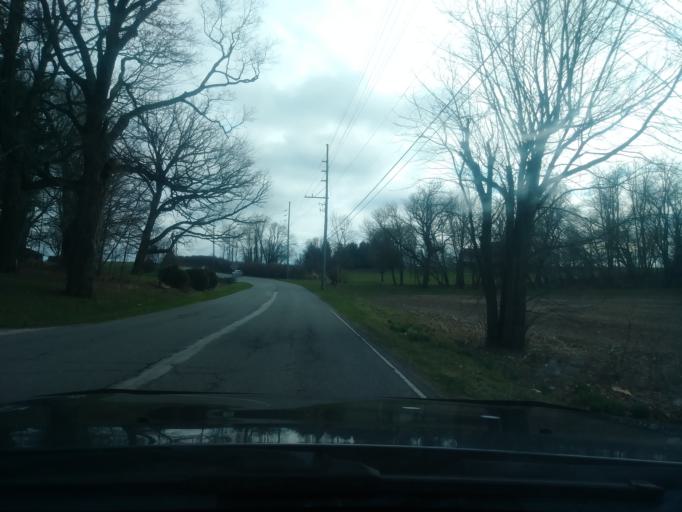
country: US
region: Indiana
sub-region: LaPorte County
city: LaPorte
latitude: 41.6151
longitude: -86.7967
